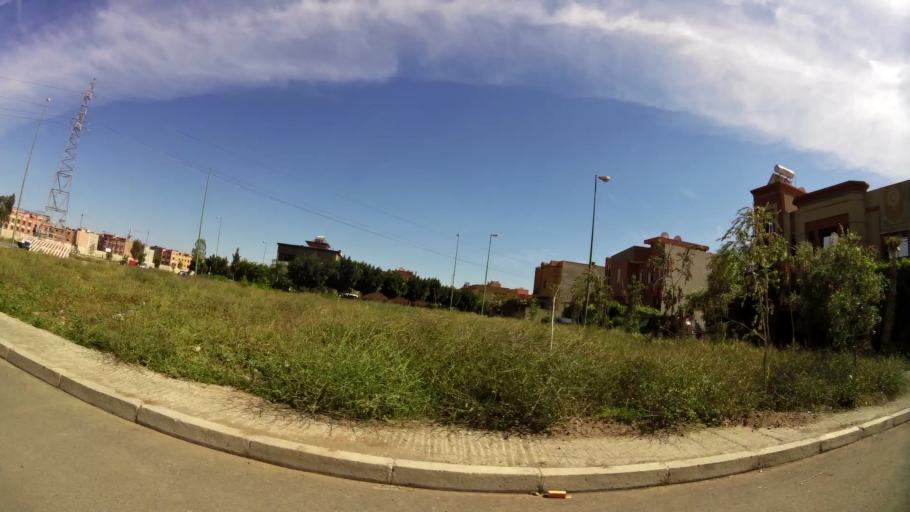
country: MA
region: Marrakech-Tensift-Al Haouz
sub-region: Marrakech
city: Marrakesh
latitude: 31.6419
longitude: -8.0425
